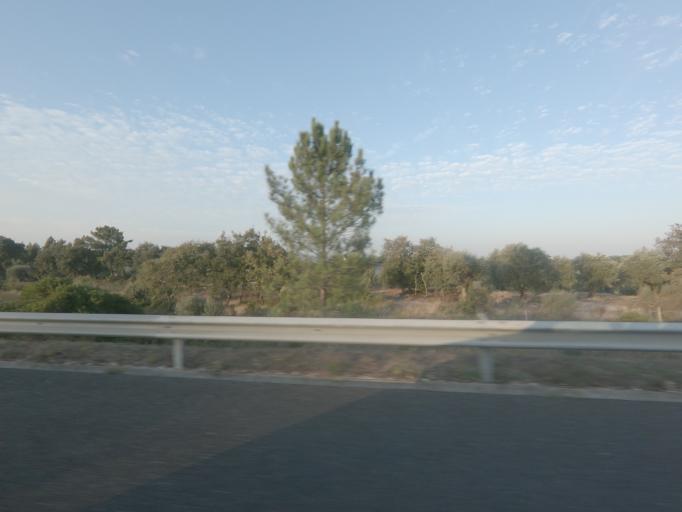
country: PT
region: Leiria
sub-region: Leiria
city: Santa Catarina da Serra
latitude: 39.6869
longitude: -8.6880
